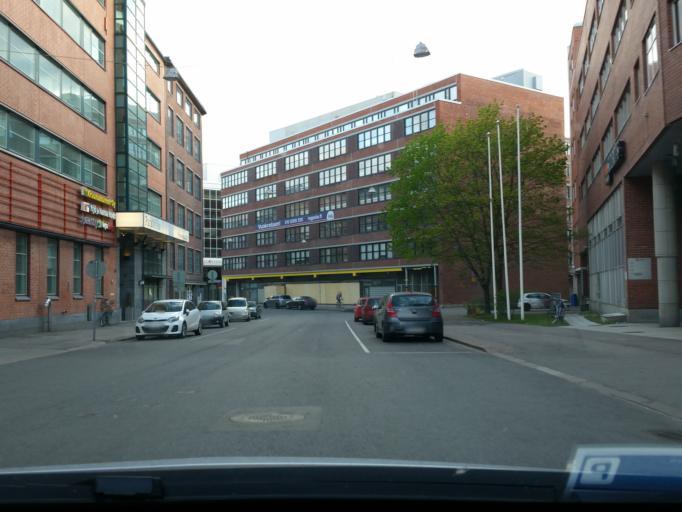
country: FI
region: Uusimaa
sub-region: Helsinki
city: Helsinki
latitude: 60.1976
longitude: 24.9480
